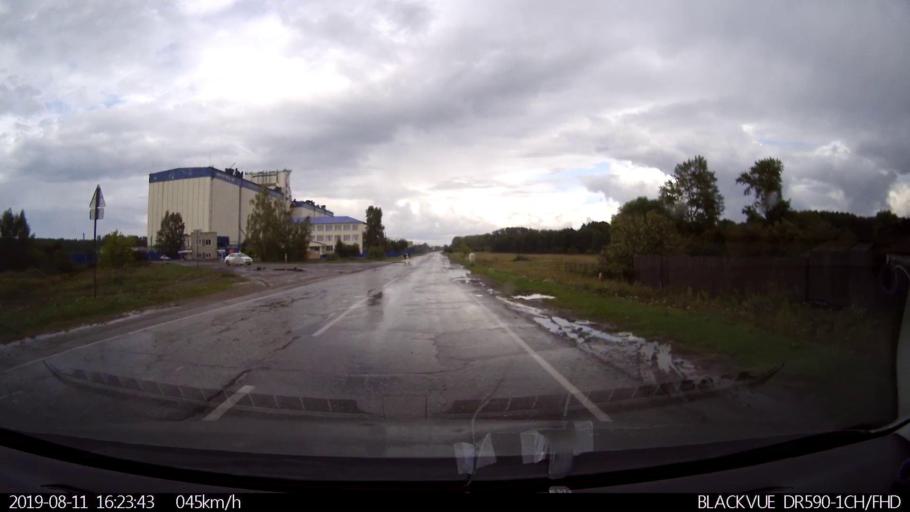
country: RU
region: Ulyanovsk
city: Mayna
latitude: 54.0969
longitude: 47.5891
